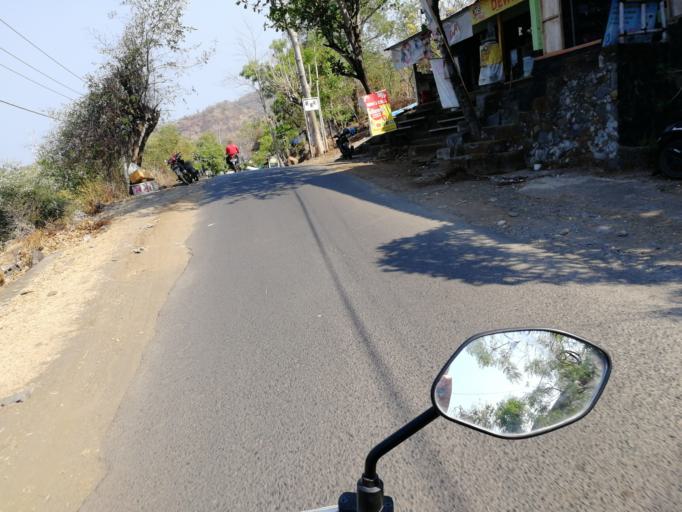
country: ID
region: Bali
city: Biaslantang Kaler
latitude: -8.3407
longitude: 115.6658
